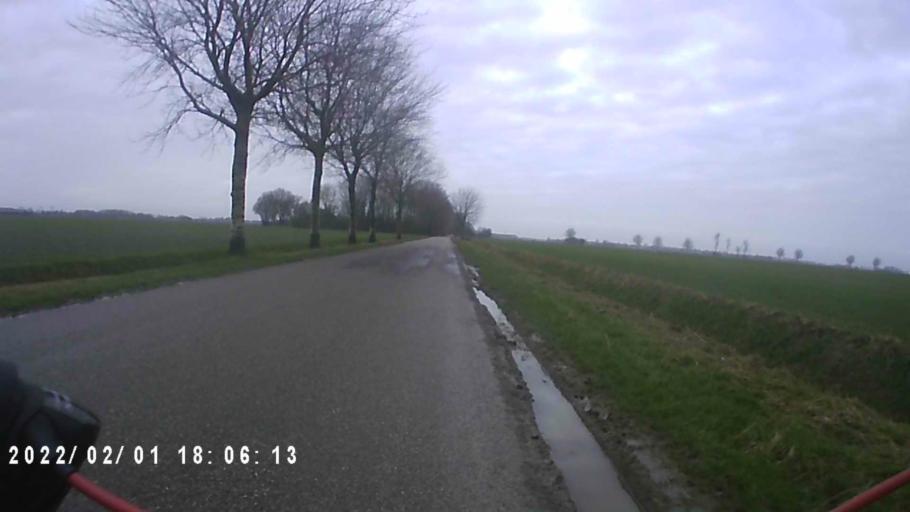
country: NL
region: Groningen
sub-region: Gemeente De Marne
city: Ulrum
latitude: 53.3407
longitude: 6.3665
